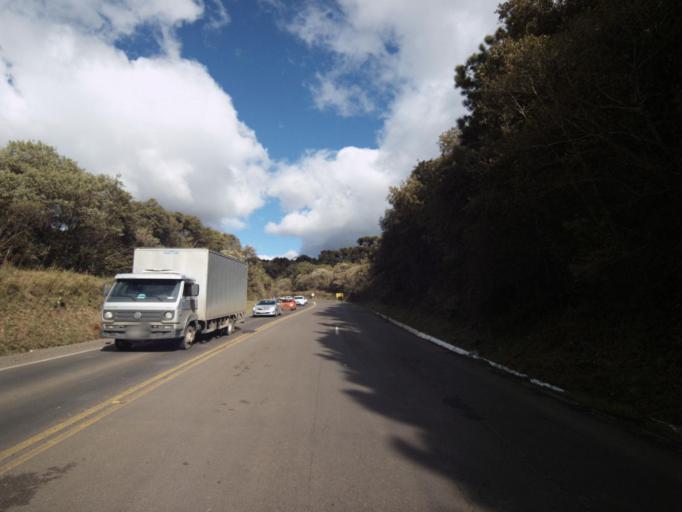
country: BR
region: Santa Catarina
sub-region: Joacaba
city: Joacaba
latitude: -27.0623
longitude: -51.6695
